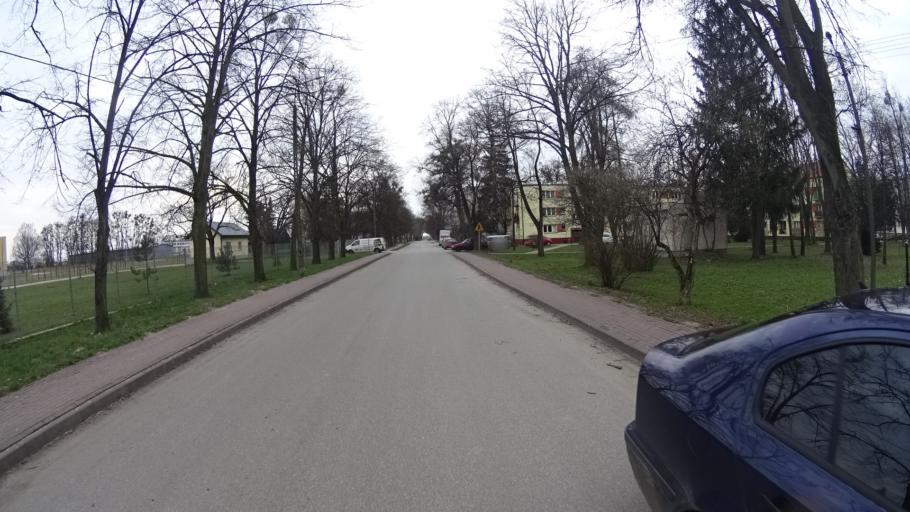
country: PL
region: Masovian Voivodeship
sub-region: Powiat warszawski zachodni
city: Blonie
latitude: 52.2152
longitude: 20.6434
